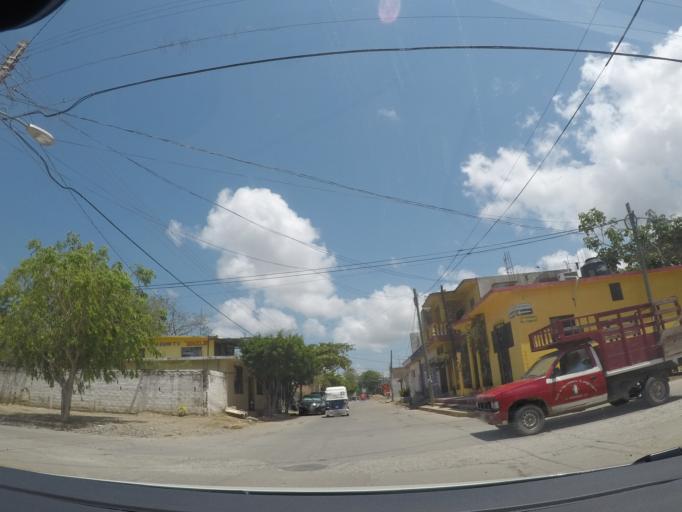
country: MX
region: Oaxaca
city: Juchitan de Zaragoza
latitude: 16.4372
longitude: -95.0161
